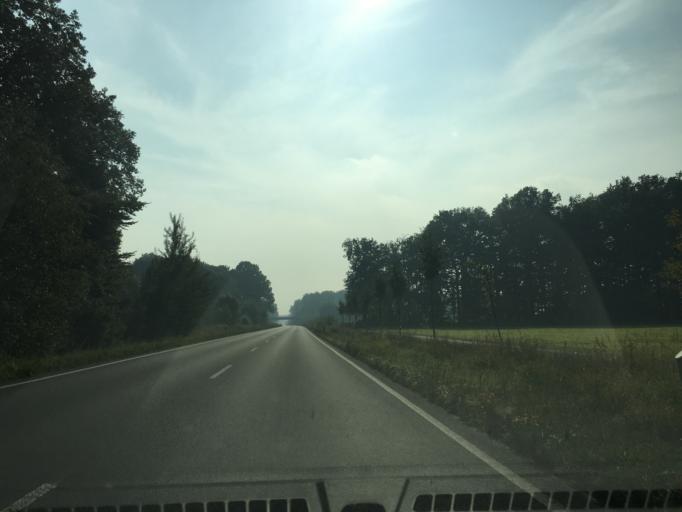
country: DE
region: North Rhine-Westphalia
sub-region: Regierungsbezirk Munster
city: Dulmen
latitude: 51.8228
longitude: 7.3328
